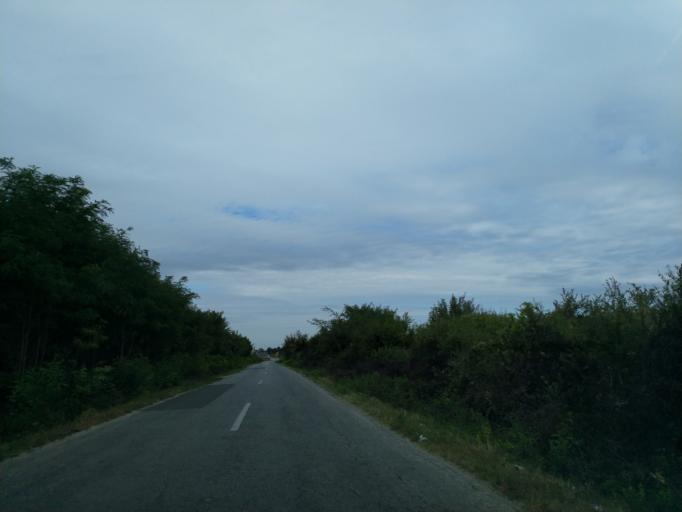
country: RS
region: Central Serbia
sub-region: Pomoravski Okrug
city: Cuprija
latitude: 43.9489
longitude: 21.3189
